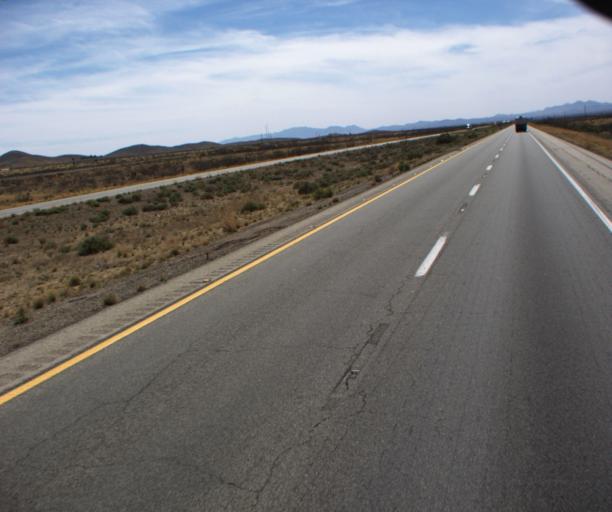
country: US
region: Arizona
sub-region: Cochise County
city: Willcox
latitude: 32.3326
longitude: -109.7659
